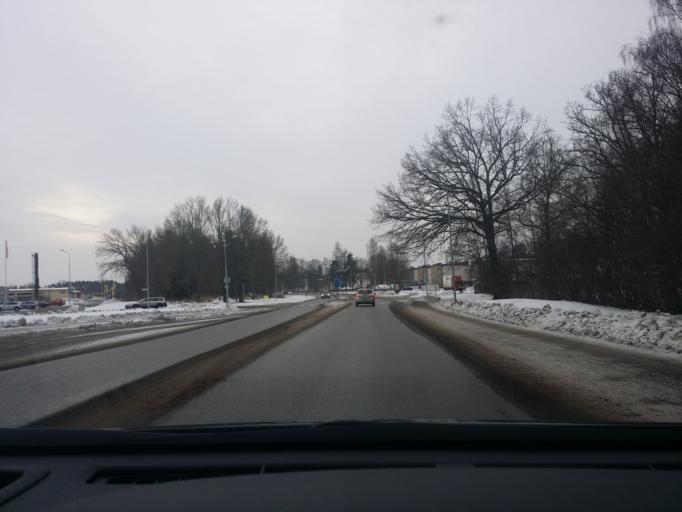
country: SE
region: Vaestra Goetaland
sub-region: Mariestads Kommun
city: Mariestad
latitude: 58.6981
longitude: 13.8178
